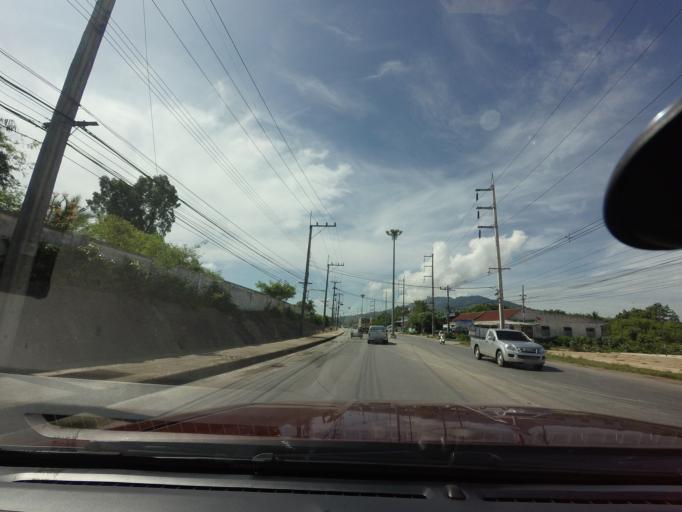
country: TH
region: Yala
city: Yala
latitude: 6.5168
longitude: 101.2700
